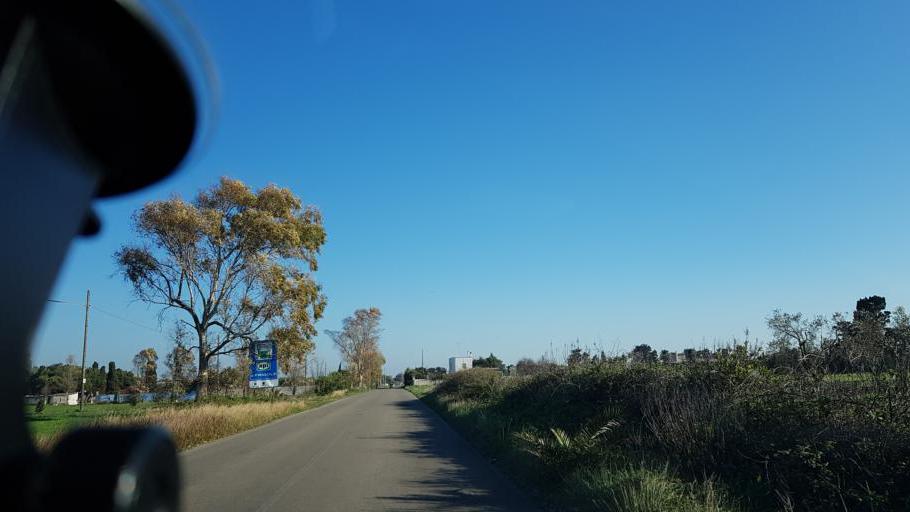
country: IT
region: Apulia
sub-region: Provincia di Lecce
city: Merine
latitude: 40.4202
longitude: 18.2488
